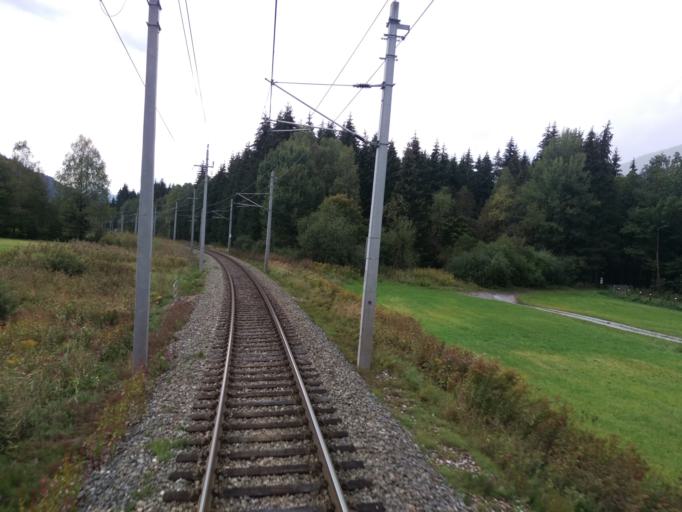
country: AT
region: Styria
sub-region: Politischer Bezirk Liezen
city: Selzthal
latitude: 47.5497
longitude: 14.2949
